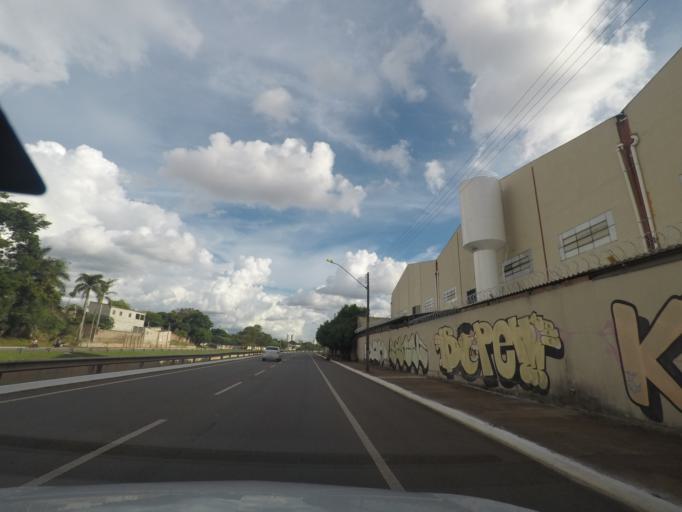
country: BR
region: Goias
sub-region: Goiania
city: Goiania
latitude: -16.6793
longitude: -49.2937
